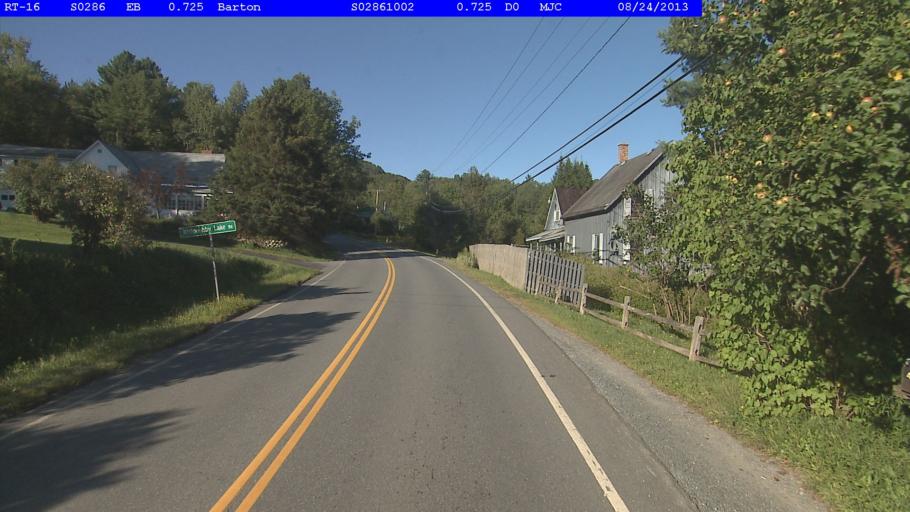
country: US
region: Vermont
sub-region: Orleans County
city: Newport
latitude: 44.7526
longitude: -72.1639
